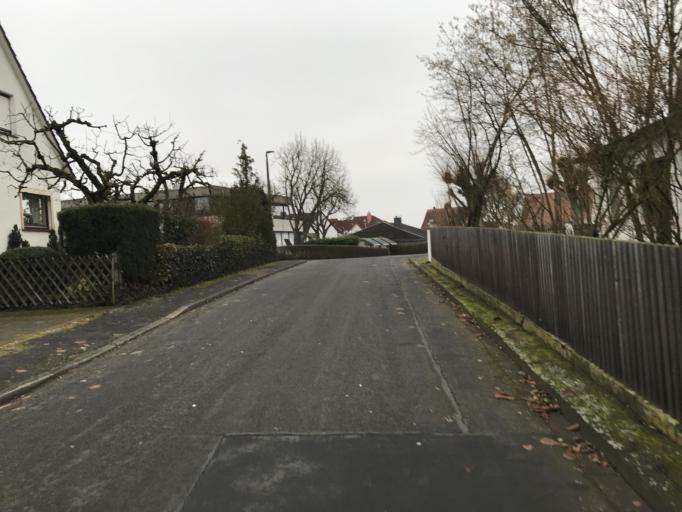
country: DE
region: Hesse
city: Fritzlar
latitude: 51.1334
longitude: 9.2661
